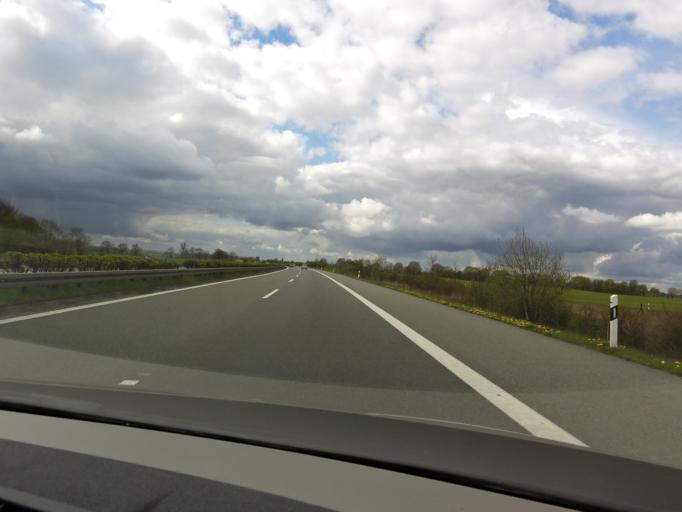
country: DE
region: Mecklenburg-Vorpommern
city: Bad Sulze
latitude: 54.0506
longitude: 12.6219
